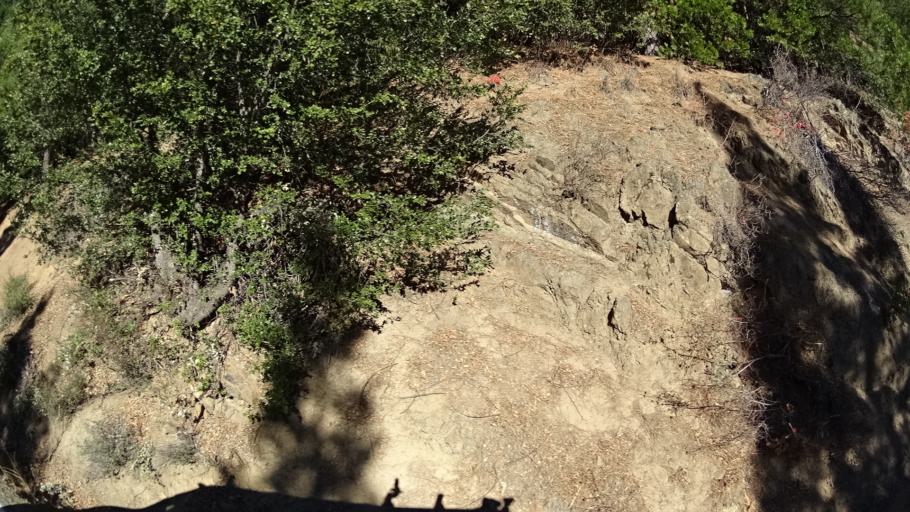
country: US
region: California
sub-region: Trinity County
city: Weaverville
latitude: 41.2243
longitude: -123.0075
